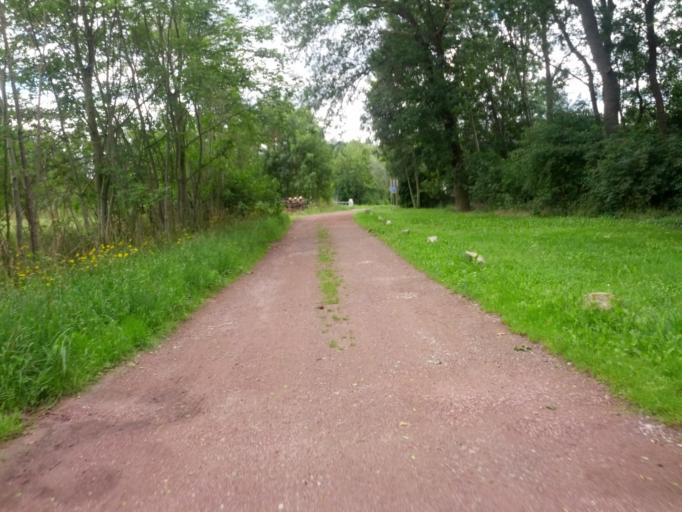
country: DE
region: Thuringia
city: Bischofroda
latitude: 50.9920
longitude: 10.3805
